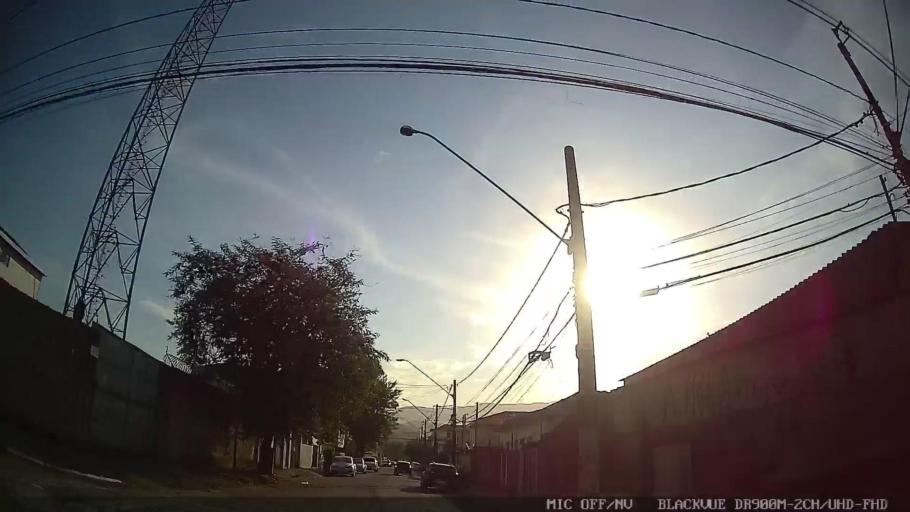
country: BR
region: Sao Paulo
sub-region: Cubatao
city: Cubatao
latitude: -23.8986
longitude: -46.4220
